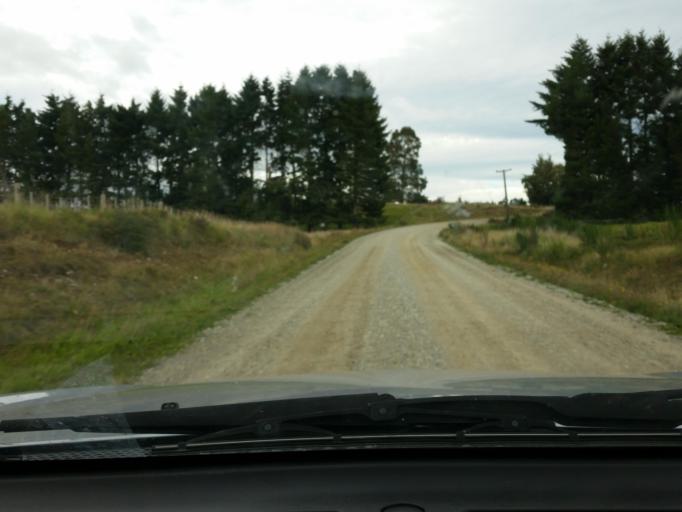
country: NZ
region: Southland
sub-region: Southland District
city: Te Anau
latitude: -45.5695
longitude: 167.7088
